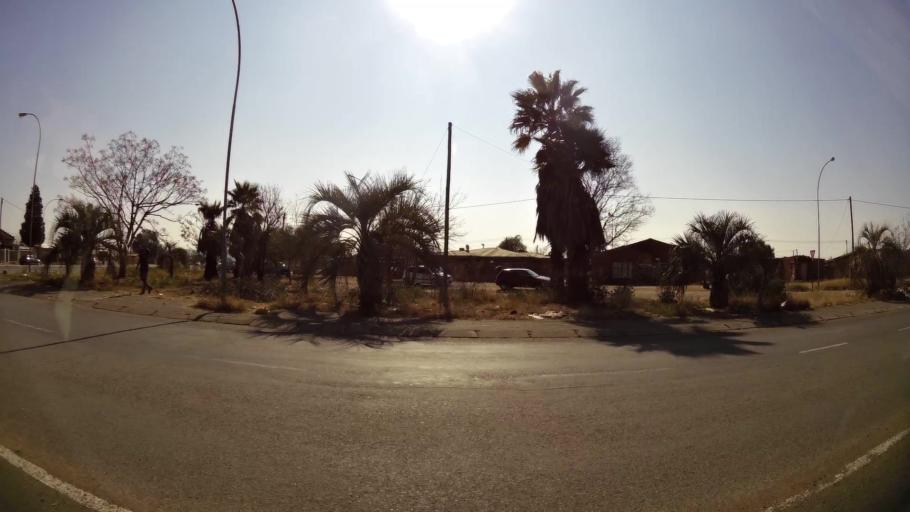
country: ZA
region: Orange Free State
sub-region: Mangaung Metropolitan Municipality
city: Bloemfontein
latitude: -29.1563
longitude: 26.2419
